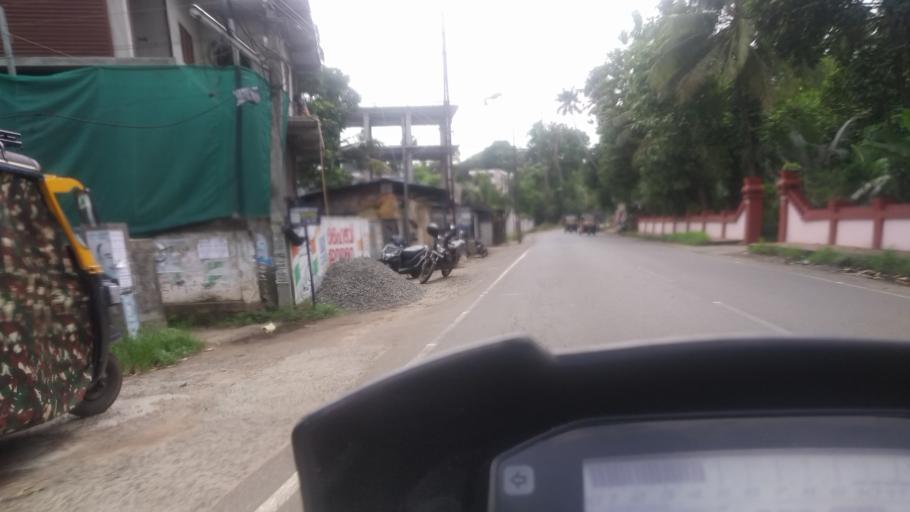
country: IN
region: Kerala
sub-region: Ernakulam
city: Aluva
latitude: 10.1207
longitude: 76.3381
